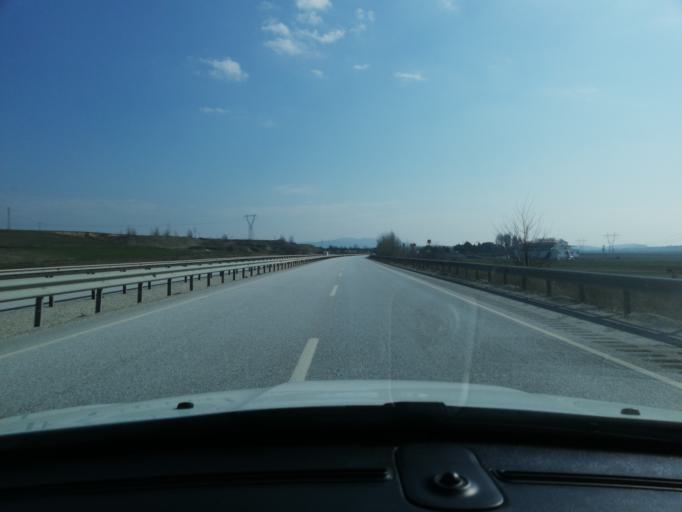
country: TR
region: Cankiri
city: Atkaracalar
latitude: 40.8396
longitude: 33.1609
